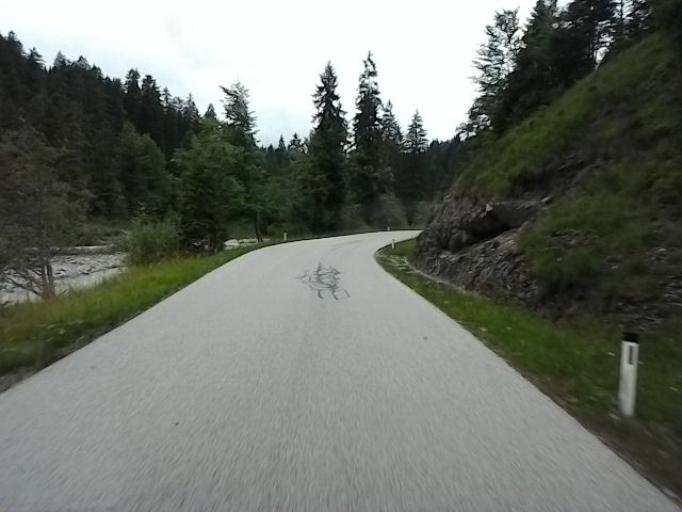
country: DE
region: Bavaria
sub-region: Upper Bavaria
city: Jachenau
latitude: 47.5079
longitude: 11.4494
